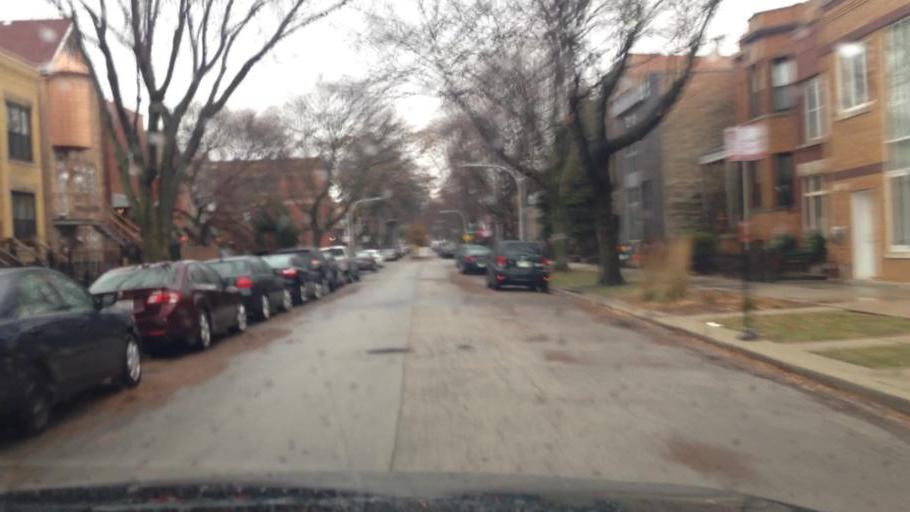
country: US
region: Illinois
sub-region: Cook County
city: Chicago
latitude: 41.8948
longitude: -87.6929
